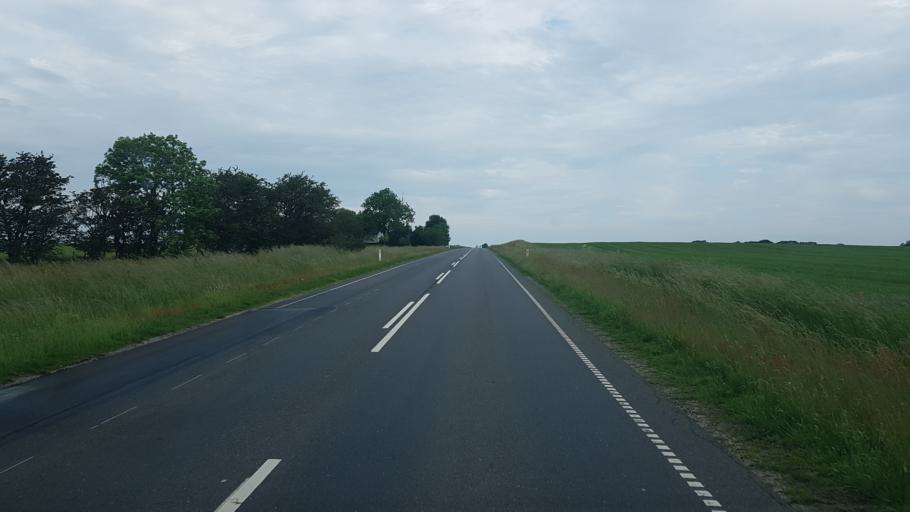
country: DK
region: South Denmark
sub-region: Vejen Kommune
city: Rodding
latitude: 55.3970
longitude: 9.0372
